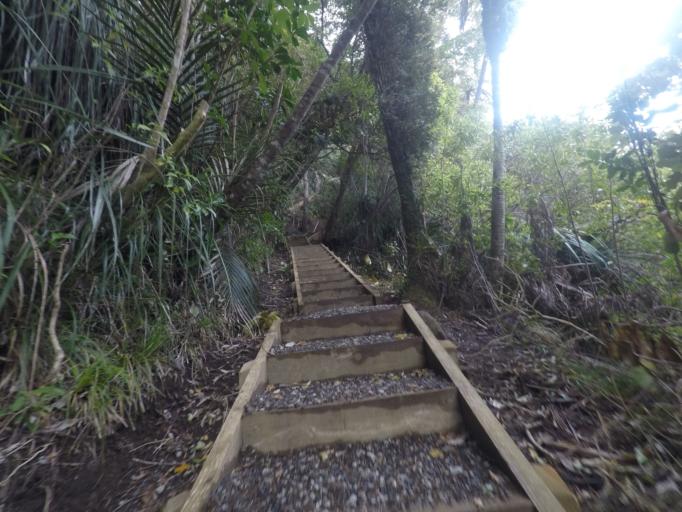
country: NZ
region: Auckland
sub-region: Auckland
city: Titirangi
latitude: -36.9999
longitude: 174.5435
